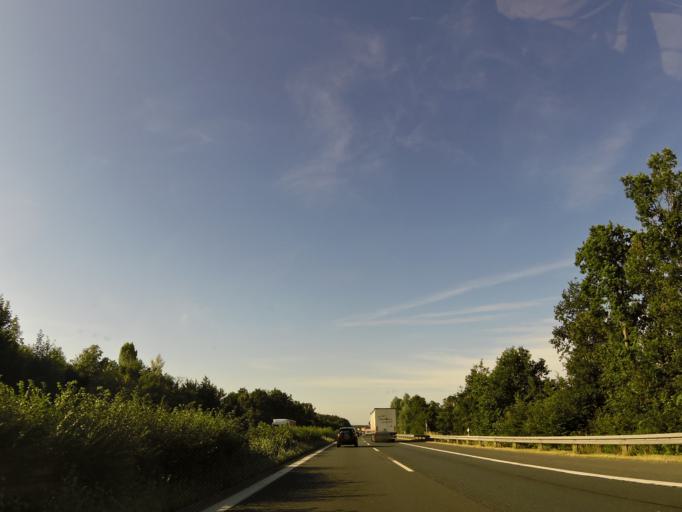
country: DE
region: Bavaria
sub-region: Regierungsbezirk Mittelfranken
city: Hessdorf
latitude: 49.6016
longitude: 10.9278
